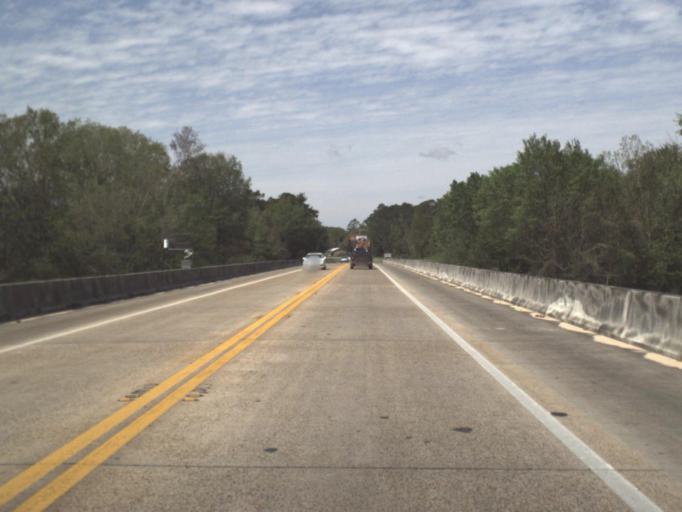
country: US
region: Florida
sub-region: Okaloosa County
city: Crestview
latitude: 30.7529
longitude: -86.6270
